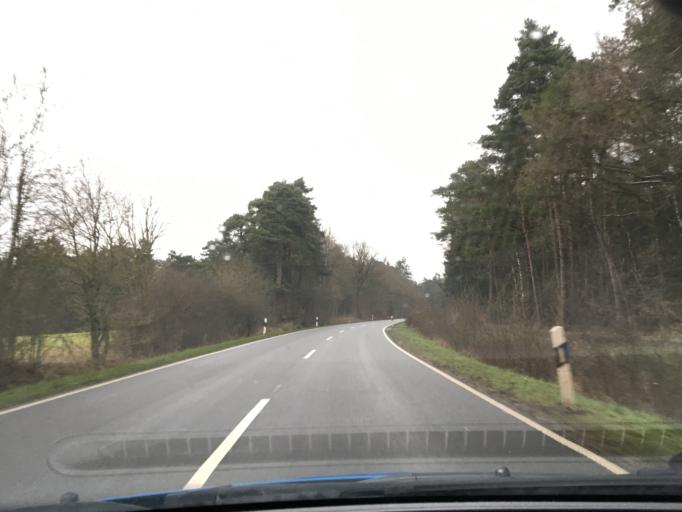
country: DE
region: Schleswig-Holstein
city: Roseburg
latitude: 53.5407
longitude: 10.6362
